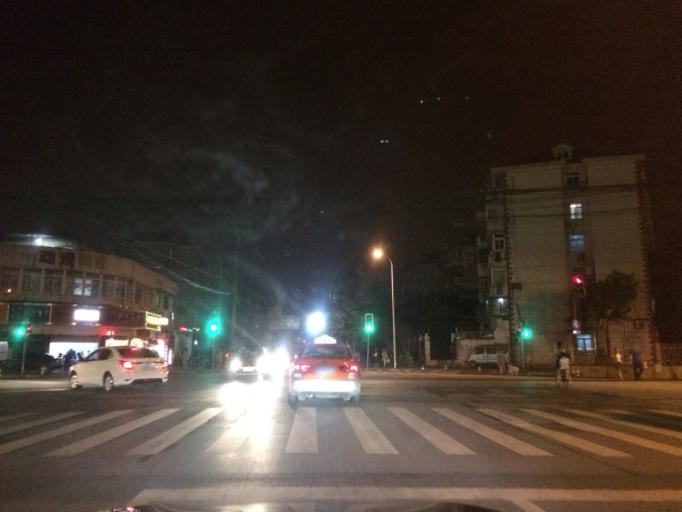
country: CN
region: Shanghai Shi
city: Baoshan
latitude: 31.4077
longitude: 121.4893
